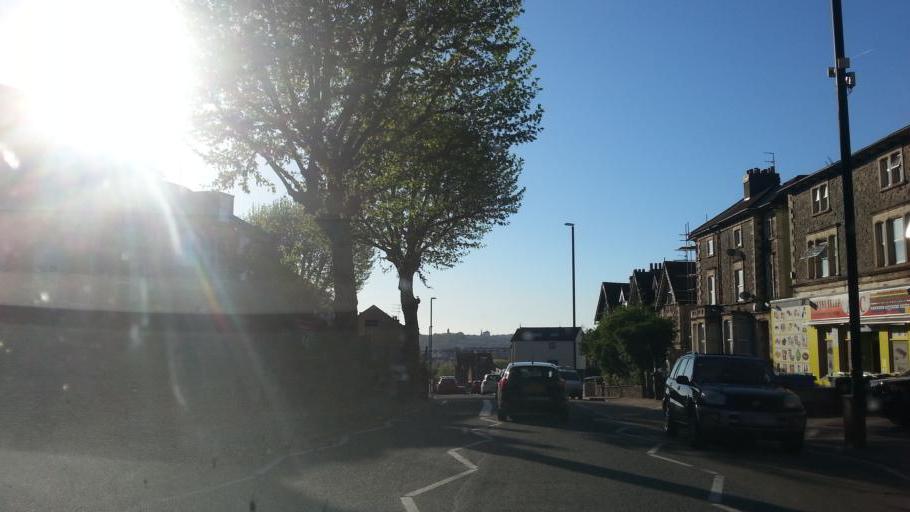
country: GB
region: England
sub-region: Bristol
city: Bristol
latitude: 51.4404
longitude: -2.5742
